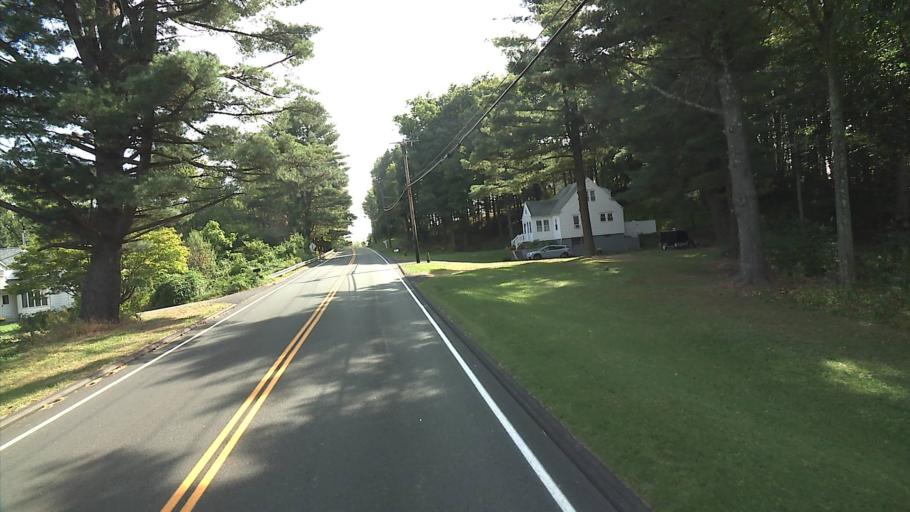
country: US
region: Connecticut
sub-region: Fairfield County
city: Newtown
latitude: 41.4137
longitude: -73.2759
